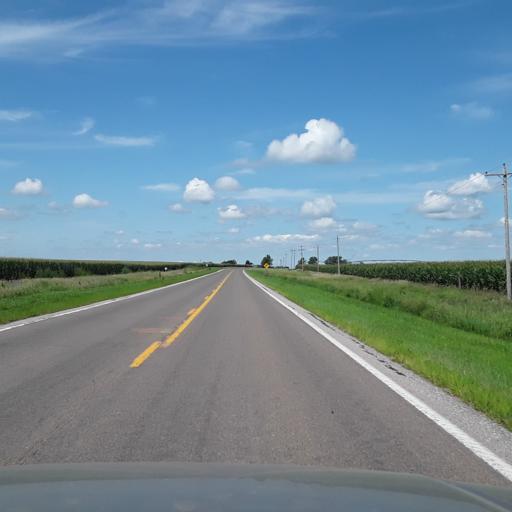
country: US
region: Nebraska
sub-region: Polk County
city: Osceola
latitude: 41.0759
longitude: -97.4171
